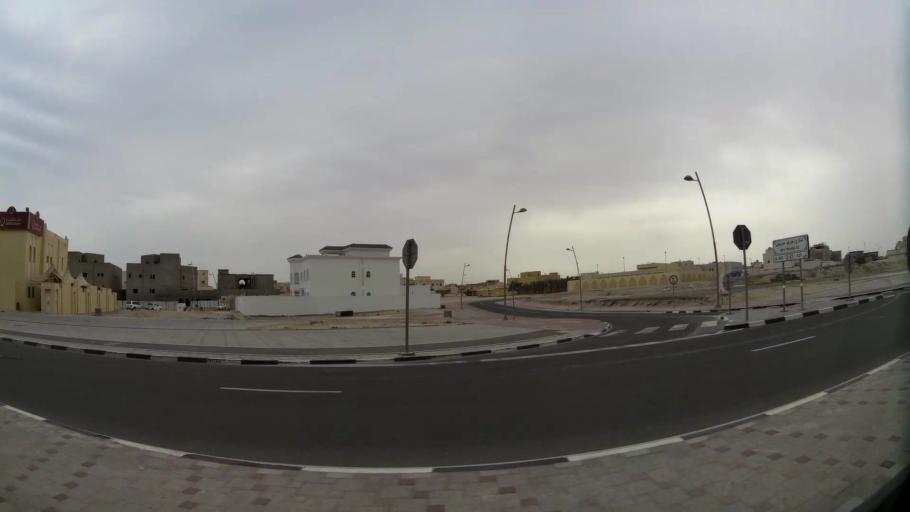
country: QA
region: Baladiyat ad Dawhah
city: Doha
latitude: 25.3451
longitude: 51.4896
